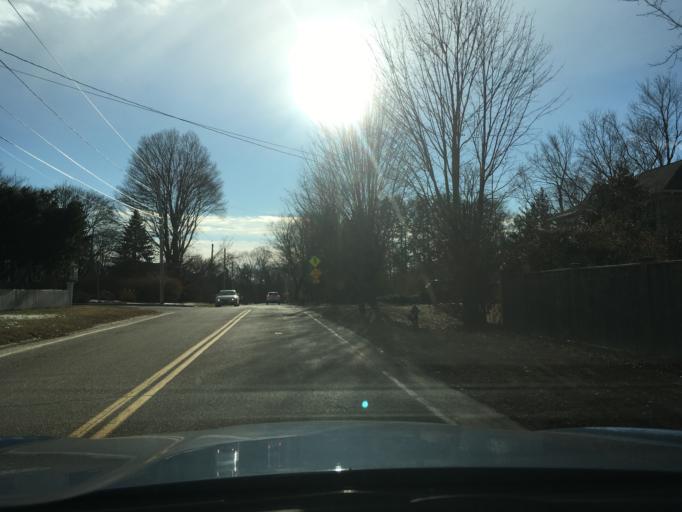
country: US
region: Rhode Island
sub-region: Kent County
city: East Greenwich
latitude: 41.6621
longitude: -71.4594
